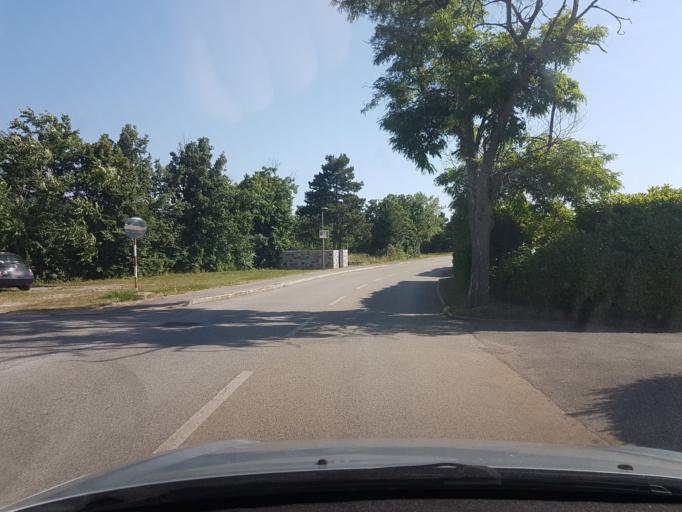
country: SI
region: Divaca
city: Divaca
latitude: 45.7447
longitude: 13.9360
